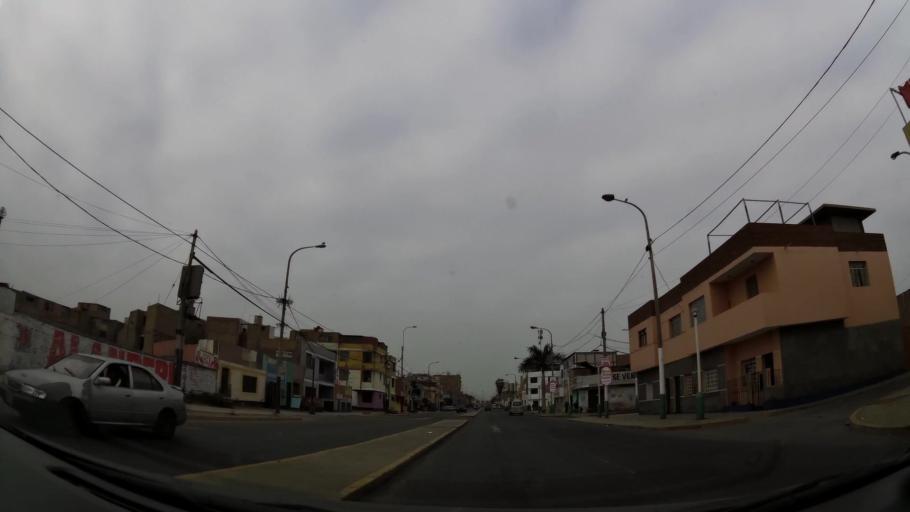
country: PE
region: Callao
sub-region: Callao
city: Callao
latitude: -12.0668
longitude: -77.1276
